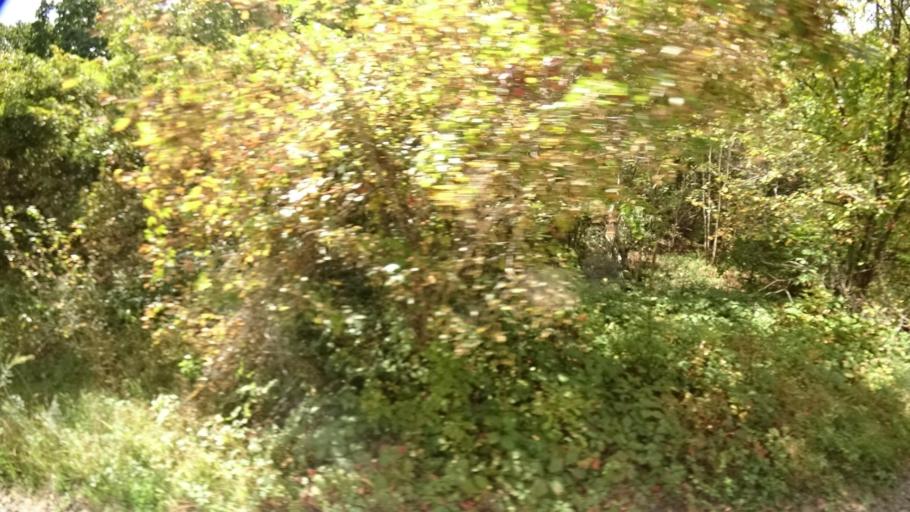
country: RU
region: Primorskiy
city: Yakovlevka
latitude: 44.6503
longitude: 133.5896
